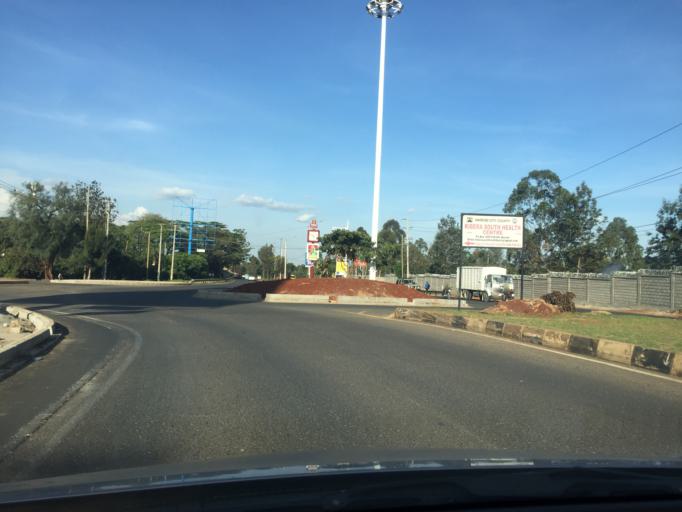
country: KE
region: Nairobi Area
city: Nairobi
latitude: -1.3330
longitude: 36.7813
